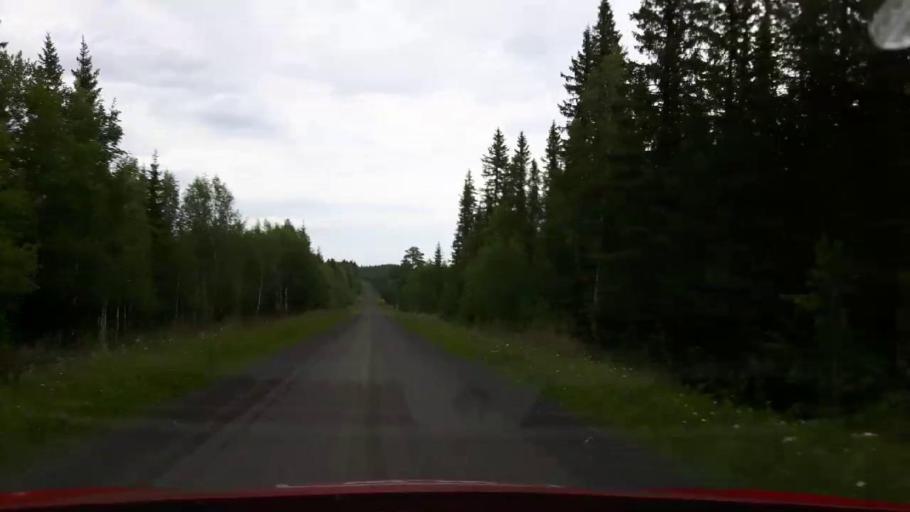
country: SE
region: Jaemtland
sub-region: OEstersunds Kommun
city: Lit
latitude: 63.3932
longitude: 15.2175
